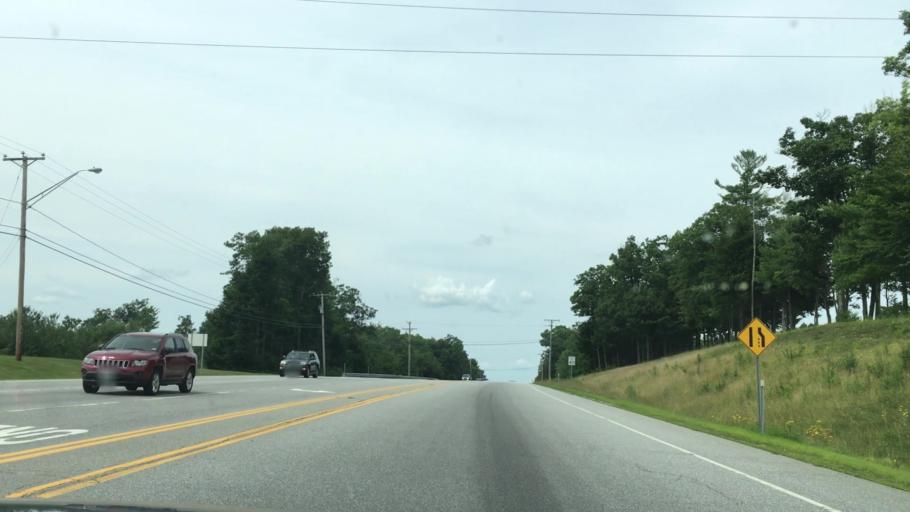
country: US
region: New Hampshire
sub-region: Cheshire County
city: Rindge
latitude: 42.7421
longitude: -72.0374
